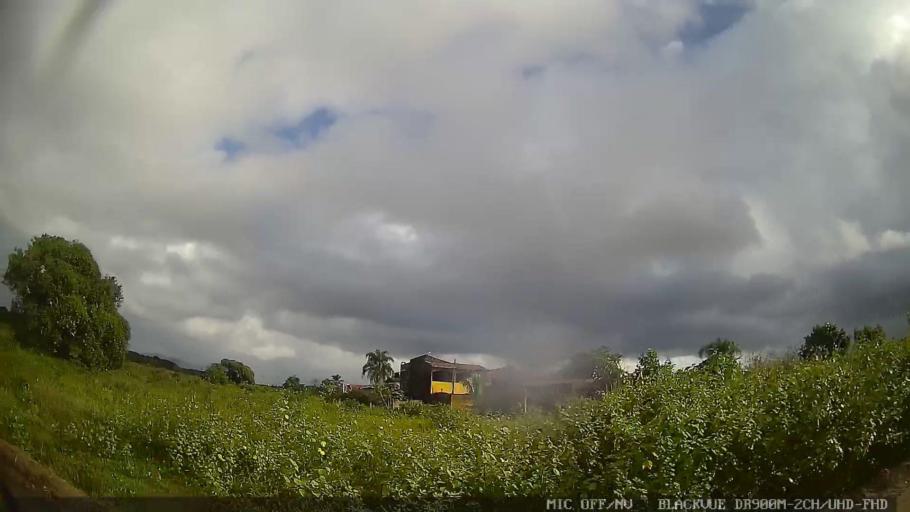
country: BR
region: Sao Paulo
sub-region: Itanhaem
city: Itanhaem
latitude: -24.2445
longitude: -46.8969
